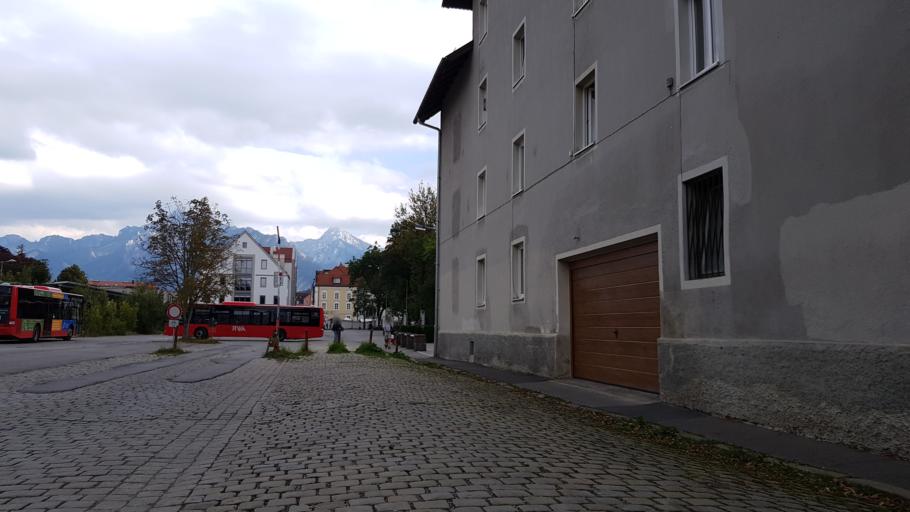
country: DE
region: Bavaria
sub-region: Swabia
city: Fuessen
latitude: 47.5707
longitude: 10.6958
